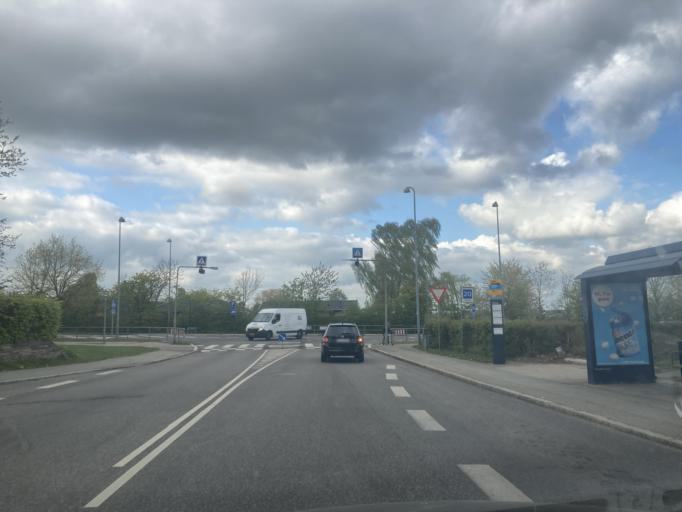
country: DK
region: Zealand
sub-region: Greve Kommune
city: Tune
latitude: 55.5956
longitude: 12.1745
